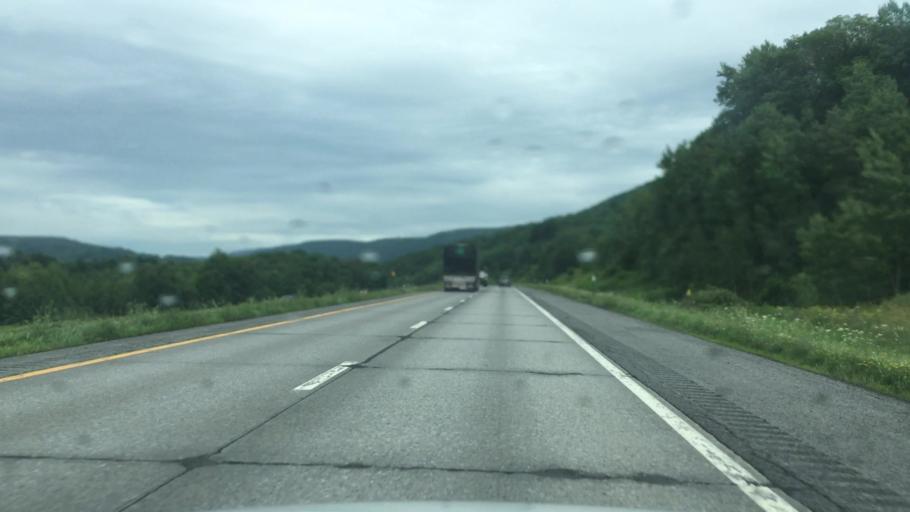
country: US
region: New York
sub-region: Otsego County
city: Worcester
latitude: 42.5864
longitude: -74.7471
